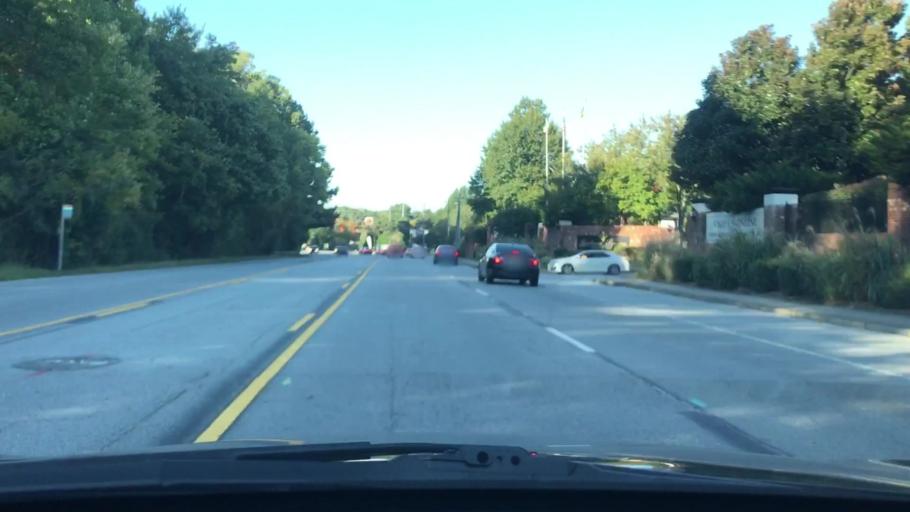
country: US
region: Georgia
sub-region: DeKalb County
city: Scottdale
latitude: 33.7896
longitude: -84.2763
